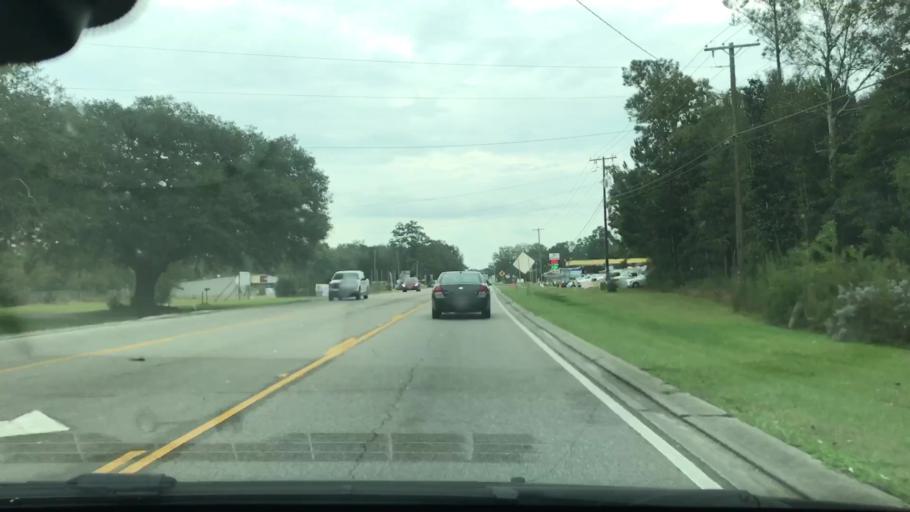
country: US
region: Louisiana
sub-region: Saint Tammany Parish
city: Pearl River
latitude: 30.3680
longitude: -89.7602
